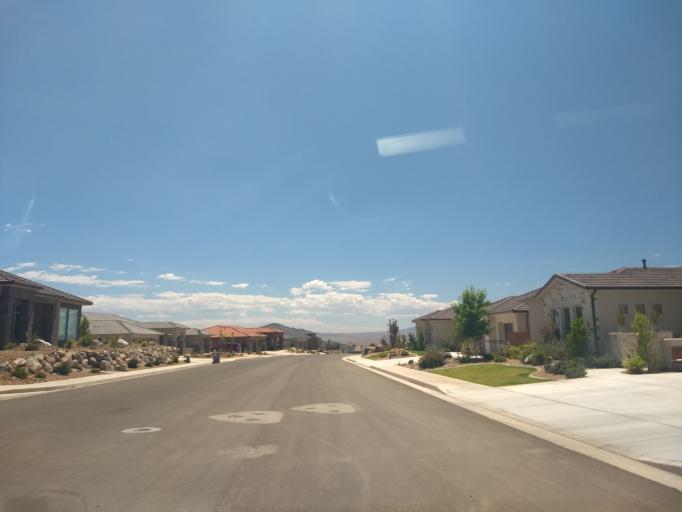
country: US
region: Utah
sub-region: Washington County
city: Washington
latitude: 37.1588
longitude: -113.5219
